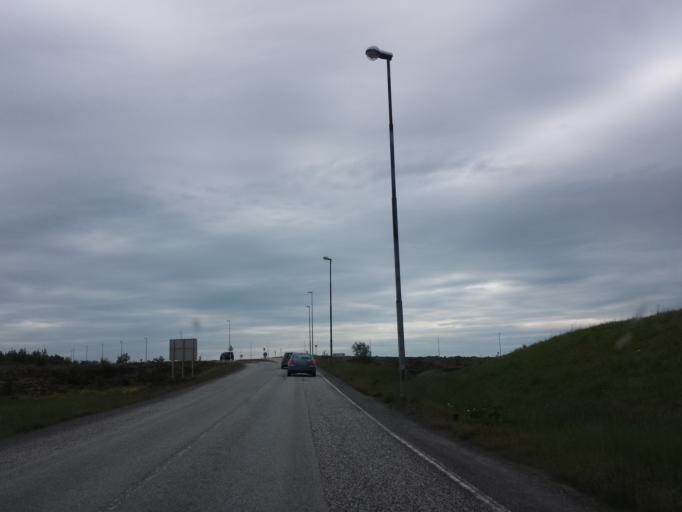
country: IS
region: Capital Region
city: Hafnarfjoerdur
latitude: 64.0845
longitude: -21.9488
